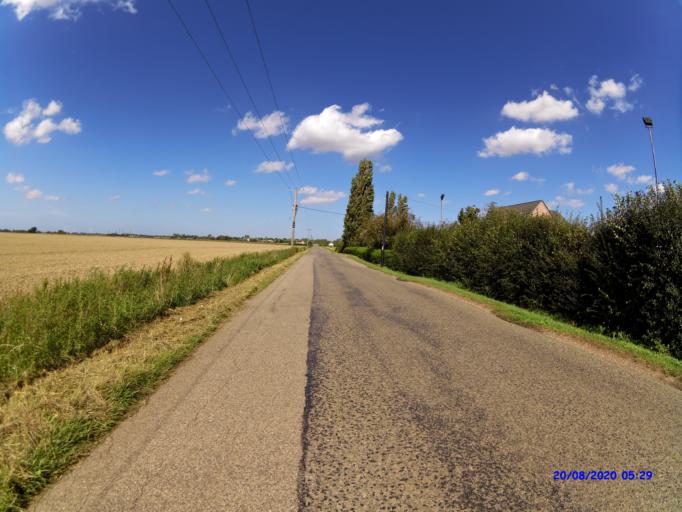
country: GB
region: England
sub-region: Cambridgeshire
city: Whittlesey
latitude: 52.5379
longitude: -0.1075
